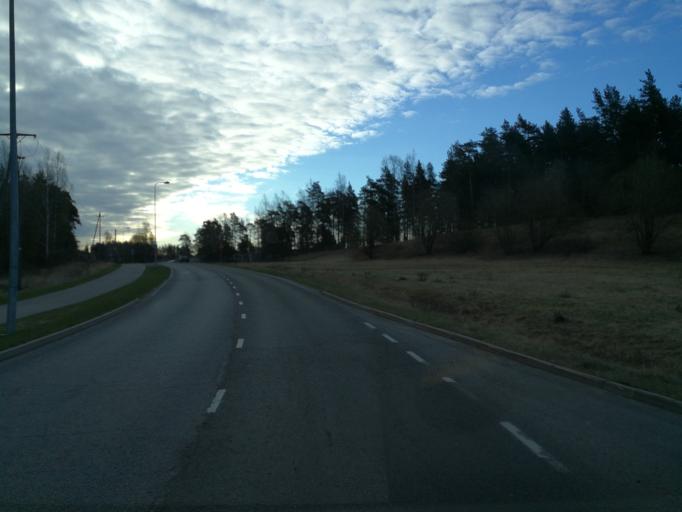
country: FI
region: Varsinais-Suomi
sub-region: Turku
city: Turku
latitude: 60.4269
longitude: 22.3145
